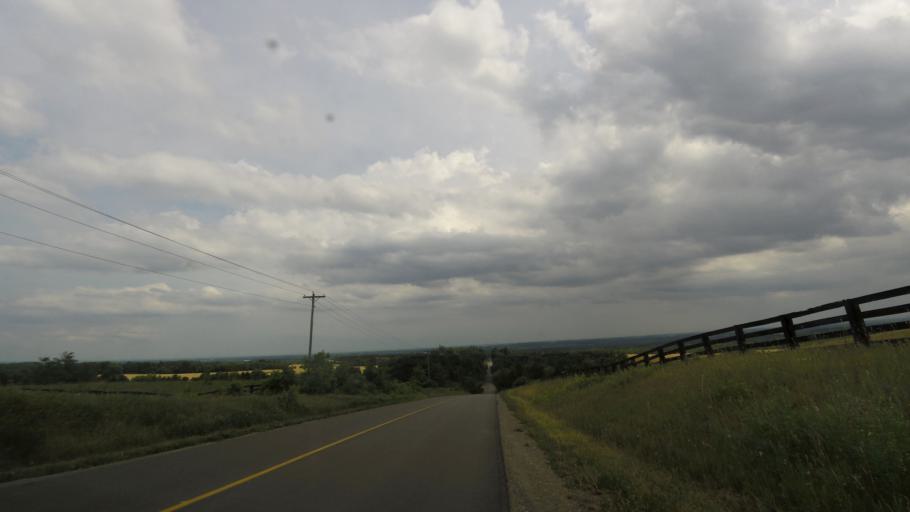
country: CA
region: Ontario
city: Orangeville
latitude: 43.8680
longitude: -79.9348
